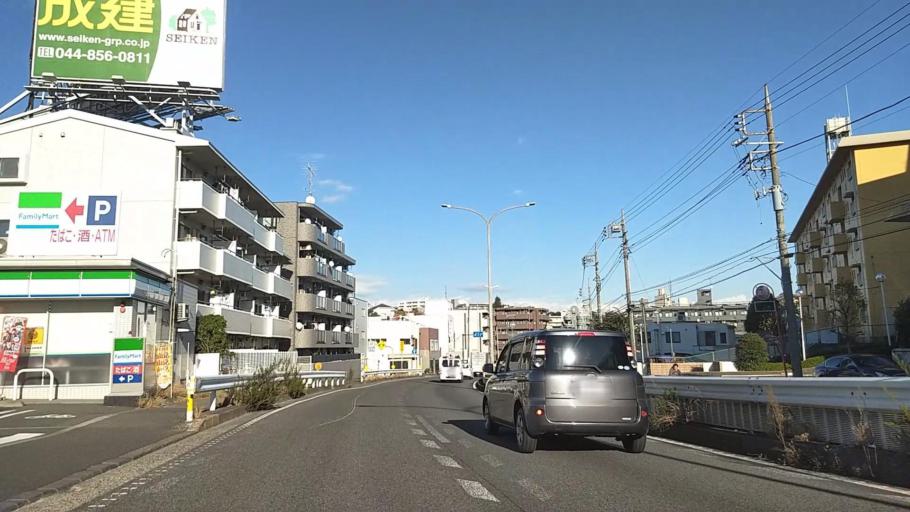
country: JP
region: Tokyo
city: Chofugaoka
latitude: 35.5743
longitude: 139.5700
